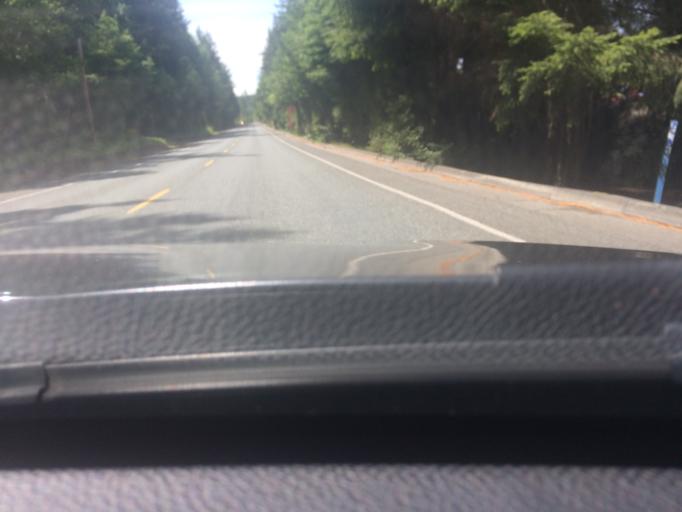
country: US
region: Washington
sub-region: Skagit County
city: Anacortes
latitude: 48.4472
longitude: -122.6587
